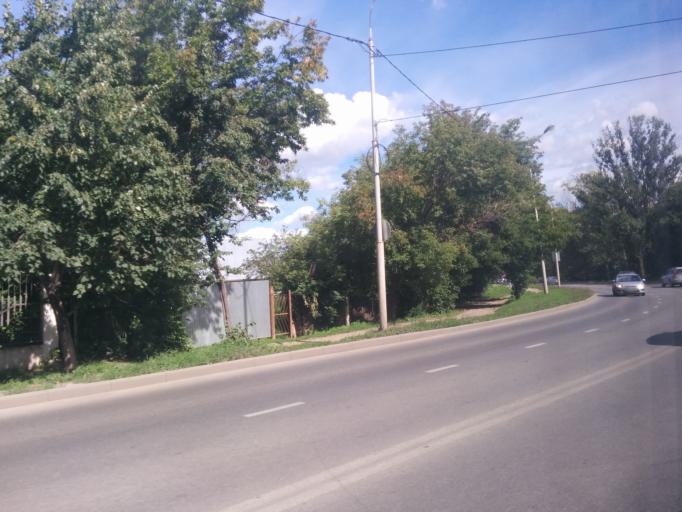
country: RU
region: Tatarstan
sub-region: Gorod Kazan'
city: Kazan
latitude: 55.7962
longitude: 49.1949
